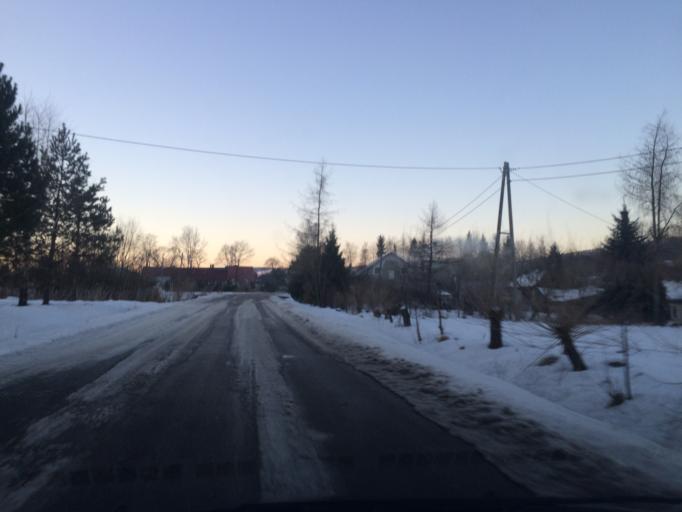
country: PL
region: Subcarpathian Voivodeship
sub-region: Powiat bieszczadzki
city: Ustrzyki Dolne
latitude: 49.4039
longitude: 22.5910
